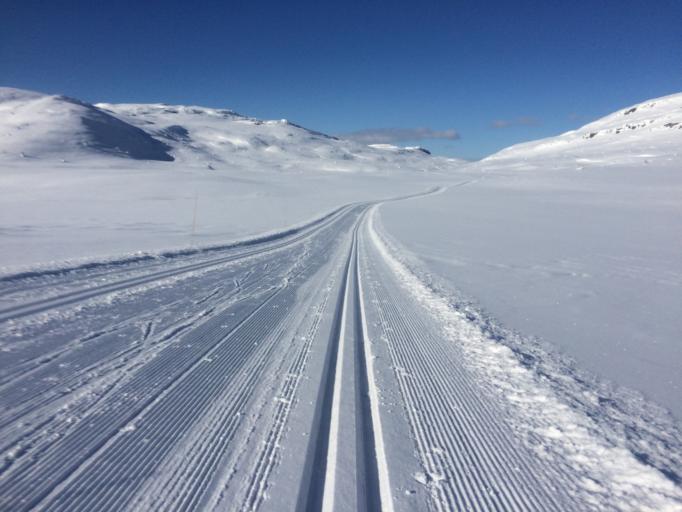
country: NO
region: Oppland
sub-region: Ringebu
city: Ringebu
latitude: 61.3798
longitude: 10.0607
